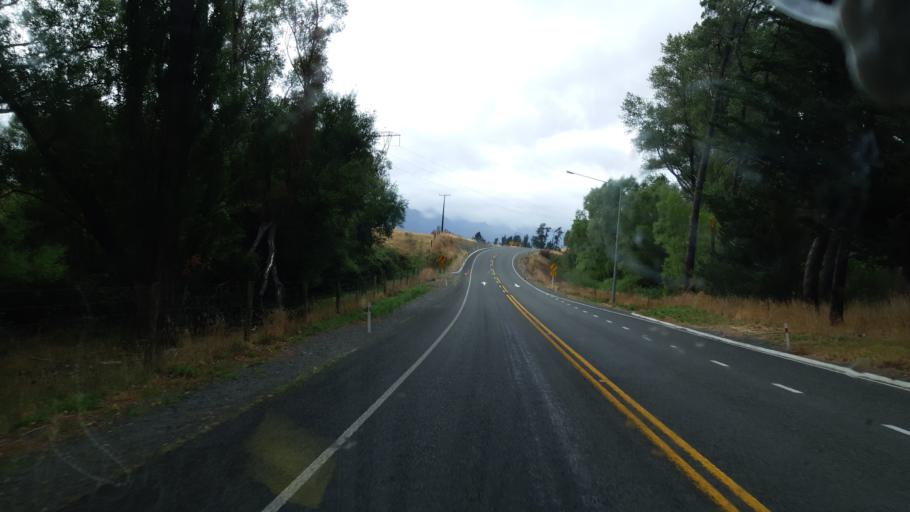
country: NZ
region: Canterbury
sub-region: Hurunui District
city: Amberley
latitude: -42.5900
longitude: 172.7771
